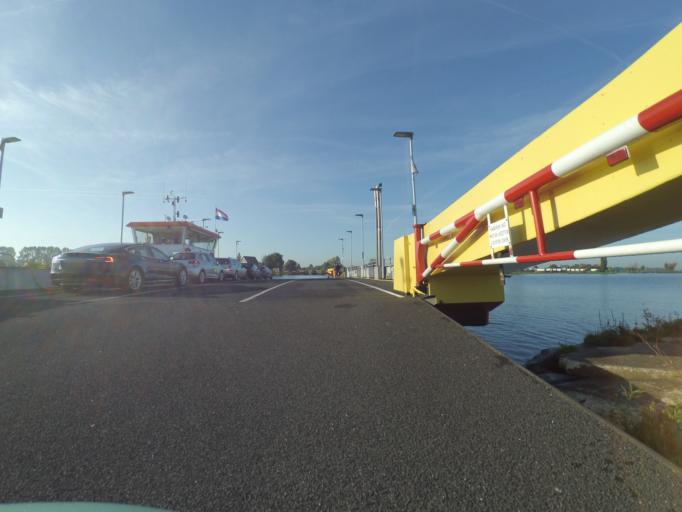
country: NL
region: Utrecht
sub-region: Gemeente Utrechtse Heuvelrug
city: Amerongen
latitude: 51.9843
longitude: 5.4567
